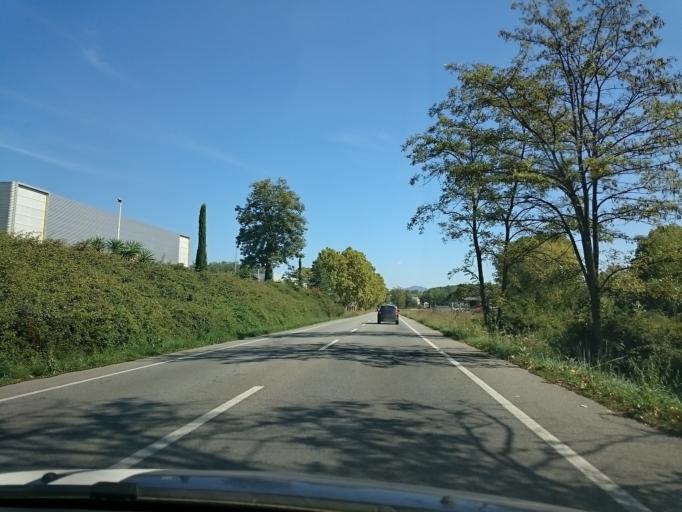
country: ES
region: Catalonia
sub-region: Provincia de Barcelona
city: Cardedeu
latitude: 41.6339
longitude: 2.3333
